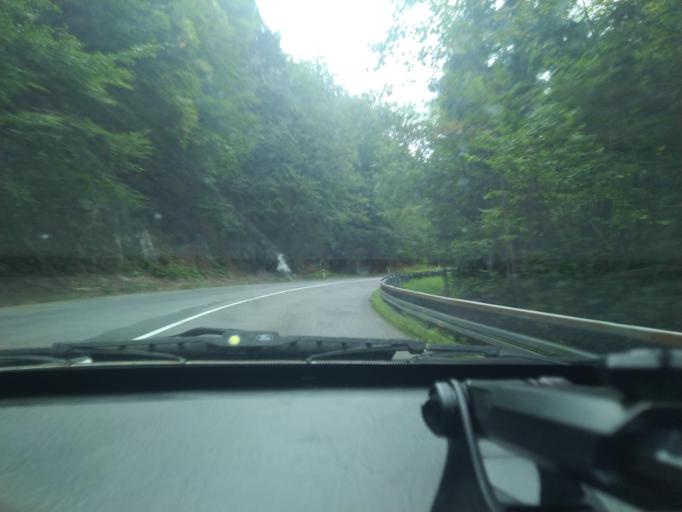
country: SK
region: Banskobystricky
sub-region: Okres Banska Bystrica
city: Banska Bystrica
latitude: 48.8223
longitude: 19.0272
